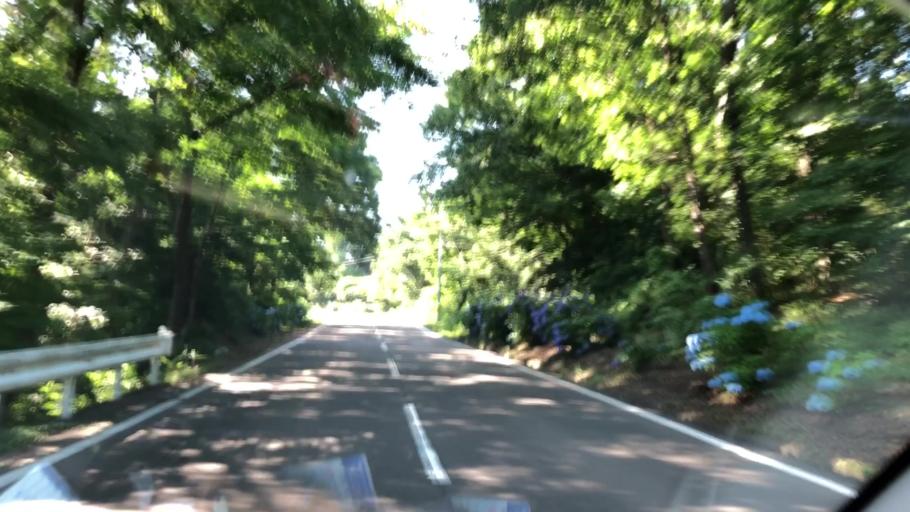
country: JP
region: Miyagi
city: Shiroishi
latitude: 38.0201
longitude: 140.5702
